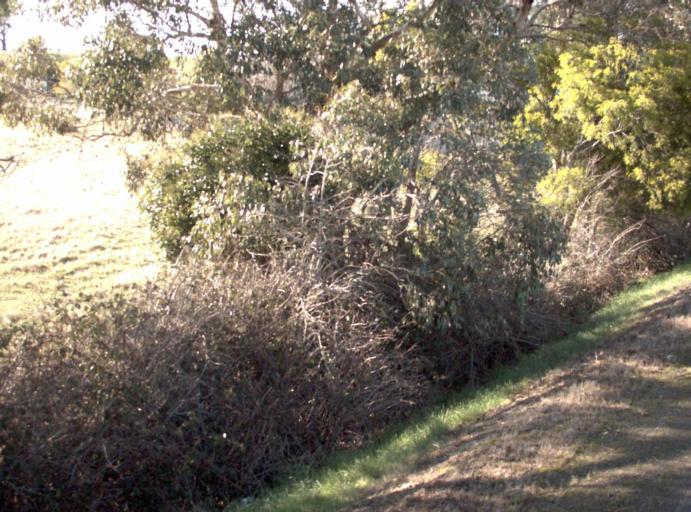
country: AU
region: Tasmania
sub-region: Launceston
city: Newstead
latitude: -41.4700
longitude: 147.2106
